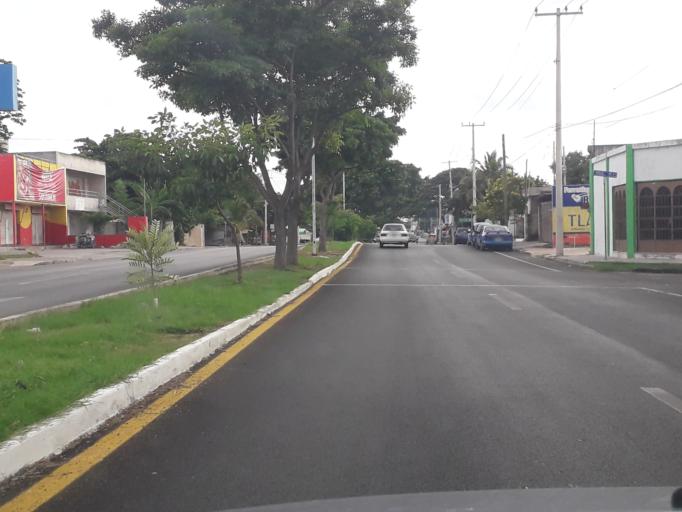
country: MX
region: Yucatan
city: Merida
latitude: 20.9664
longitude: -89.6636
